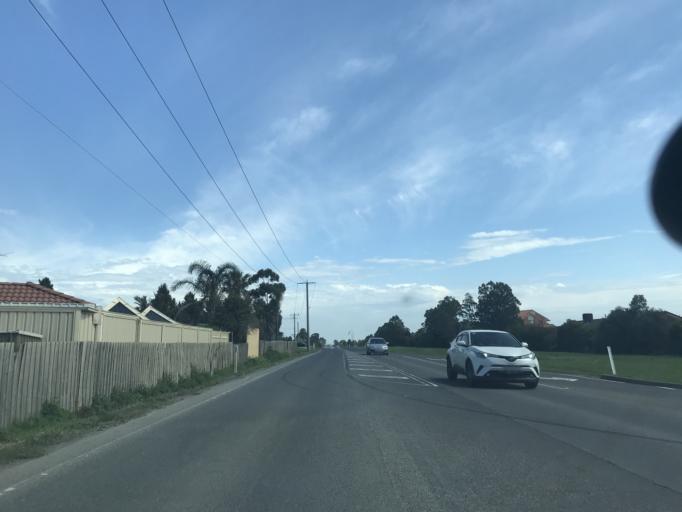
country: AU
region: Victoria
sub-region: Whittlesea
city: Epping
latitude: -37.6390
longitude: 145.0415
